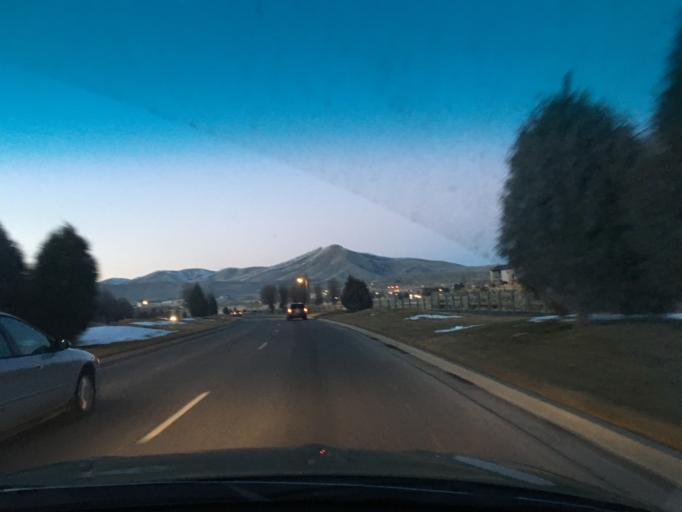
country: US
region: Utah
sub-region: Utah County
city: Eagle Mountain
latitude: 40.3745
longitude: -111.9741
